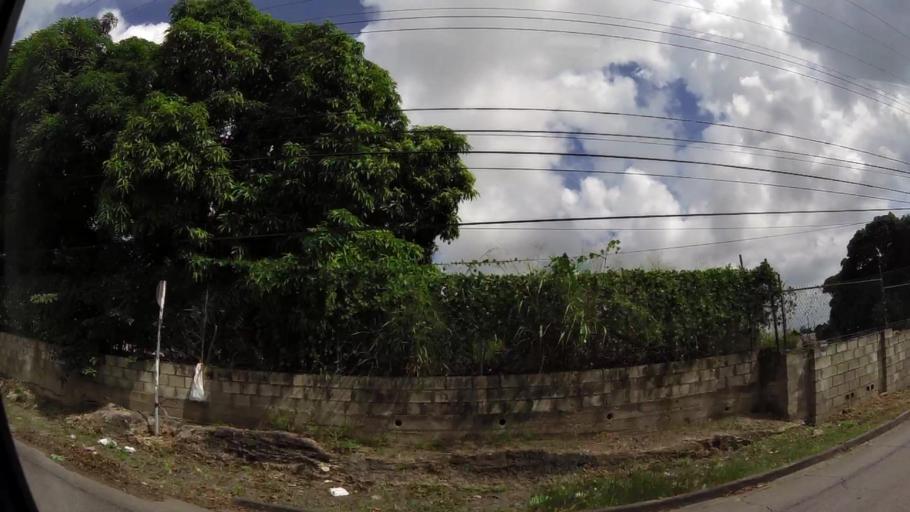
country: BB
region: Saint Michael
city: Bridgetown
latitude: 13.1204
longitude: -59.6134
